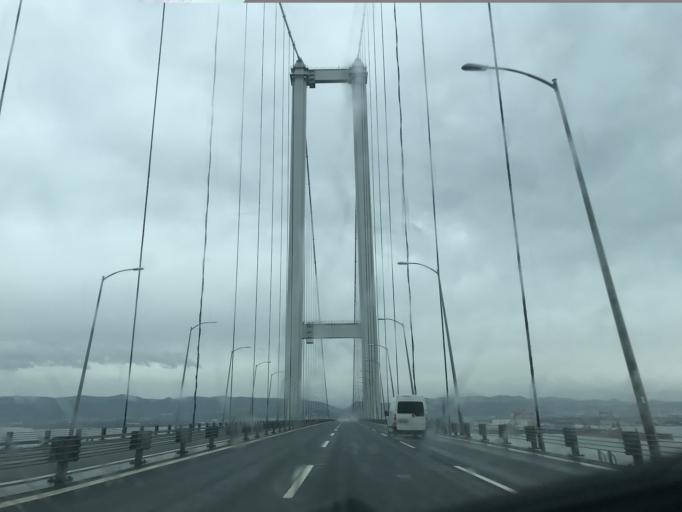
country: TR
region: Yalova
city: Altinova
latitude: 40.7505
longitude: 29.5150
